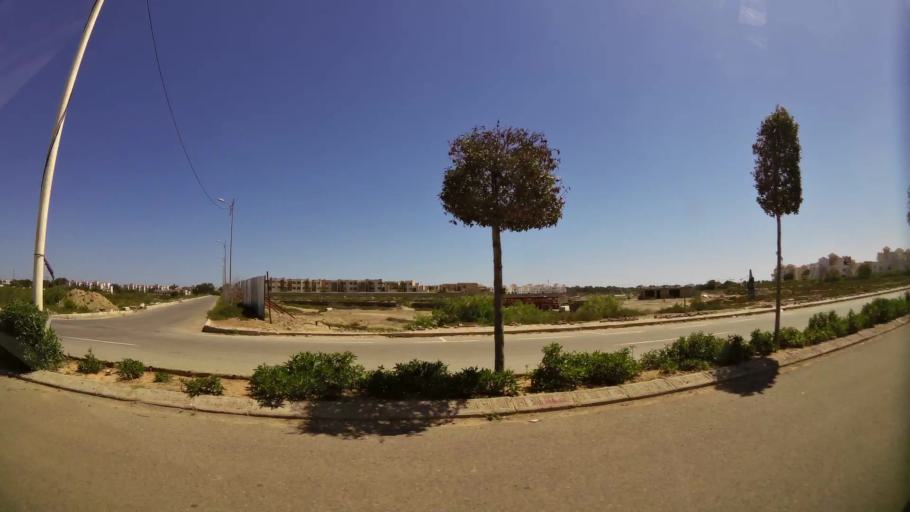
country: MA
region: Oriental
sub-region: Berkane-Taourirt
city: Madagh
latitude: 35.1060
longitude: -2.3176
